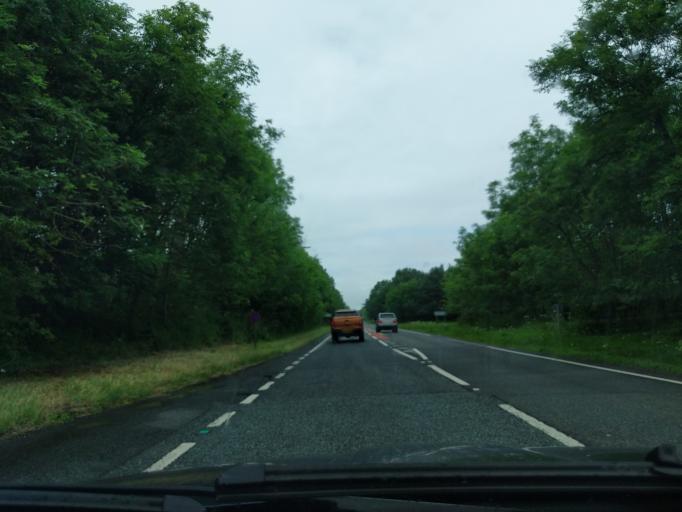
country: GB
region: England
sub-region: Northumberland
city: Belford
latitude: 55.5534
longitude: -1.7884
